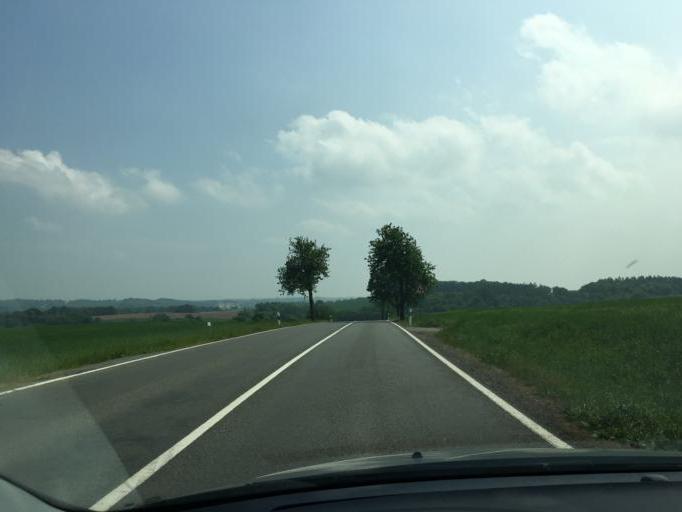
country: DE
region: Saxony
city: Colditz
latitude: 51.1459
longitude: 12.7705
